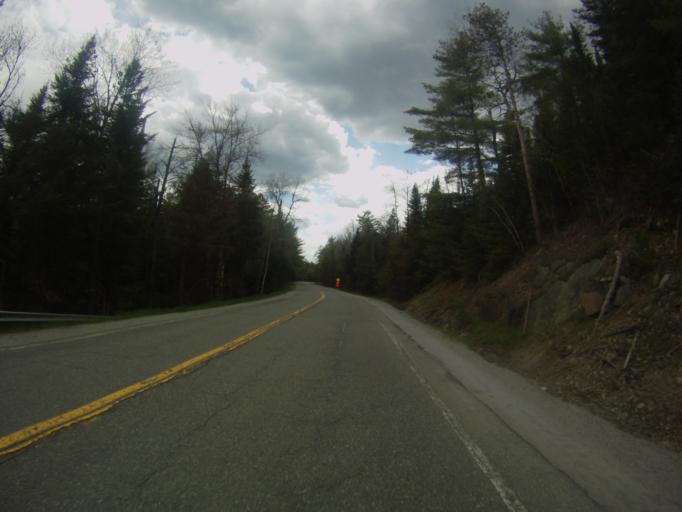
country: US
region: New York
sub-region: Essex County
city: Mineville
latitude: 44.0820
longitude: -73.5928
